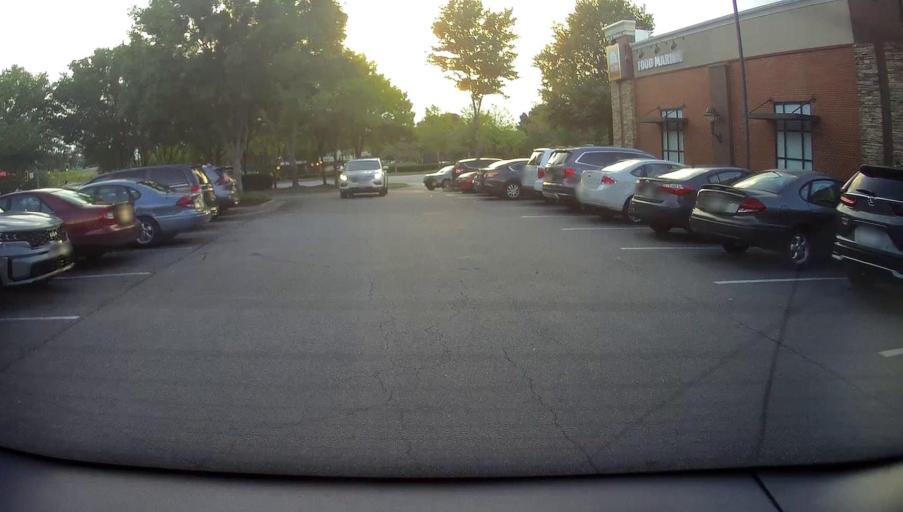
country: US
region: Georgia
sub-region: Fayette County
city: Peachtree City
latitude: 33.3974
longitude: -84.5982
